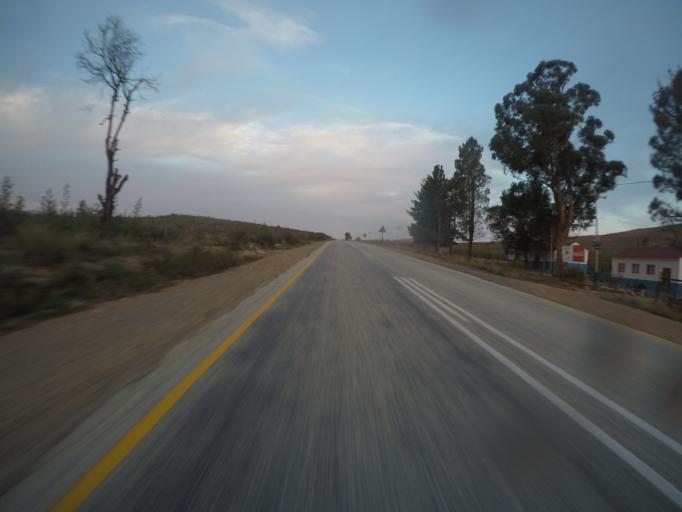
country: ZA
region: Western Cape
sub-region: Eden District Municipality
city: Plettenberg Bay
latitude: -33.7363
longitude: 23.4122
